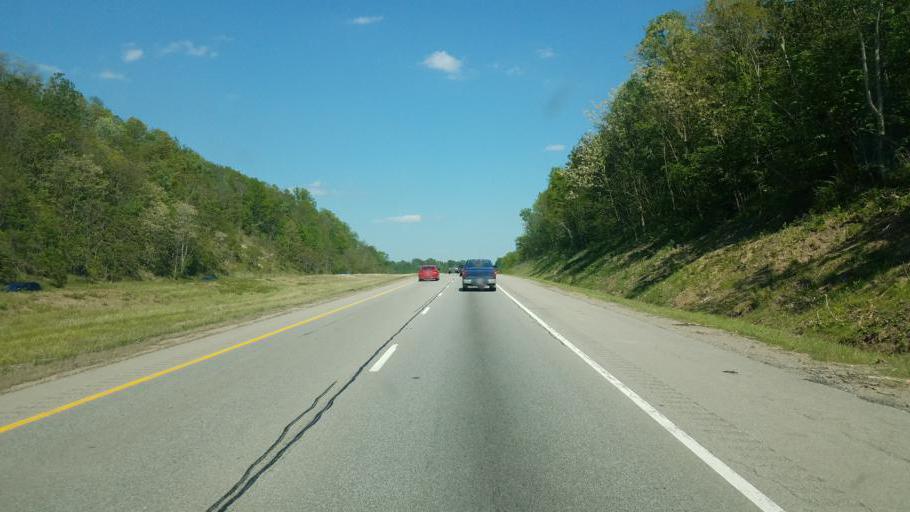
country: US
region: Ohio
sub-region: Muskingum County
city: New Concord
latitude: 39.9780
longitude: -81.7771
